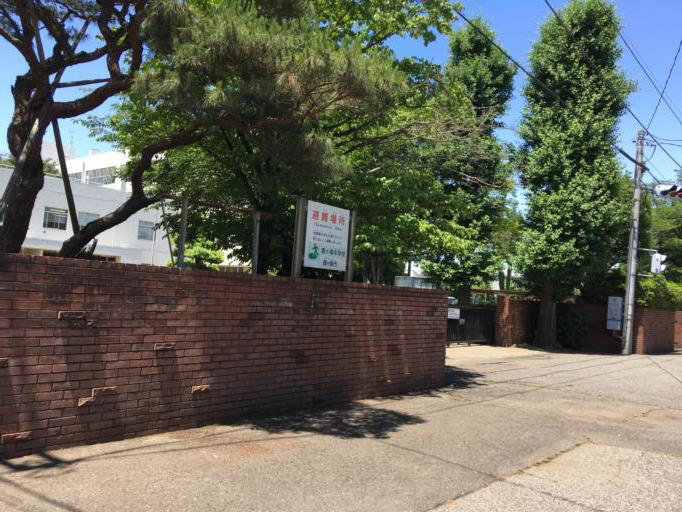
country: JP
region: Saitama
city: Sakado
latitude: 35.9357
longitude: 139.3876
